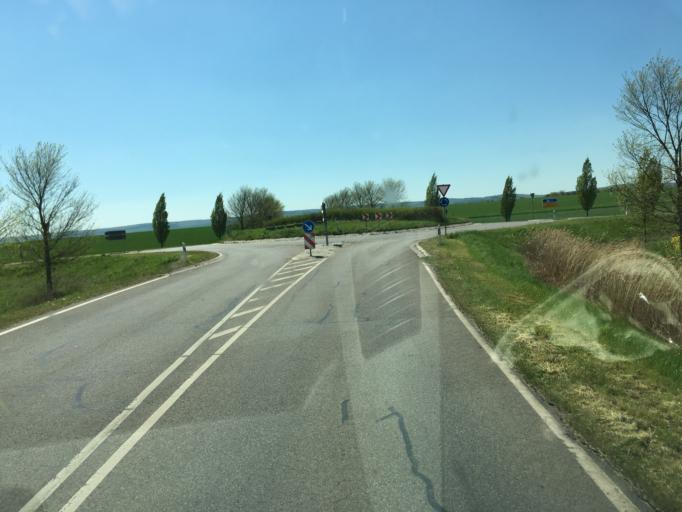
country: DE
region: Thuringia
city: Heygendorf
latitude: 51.3393
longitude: 11.3716
